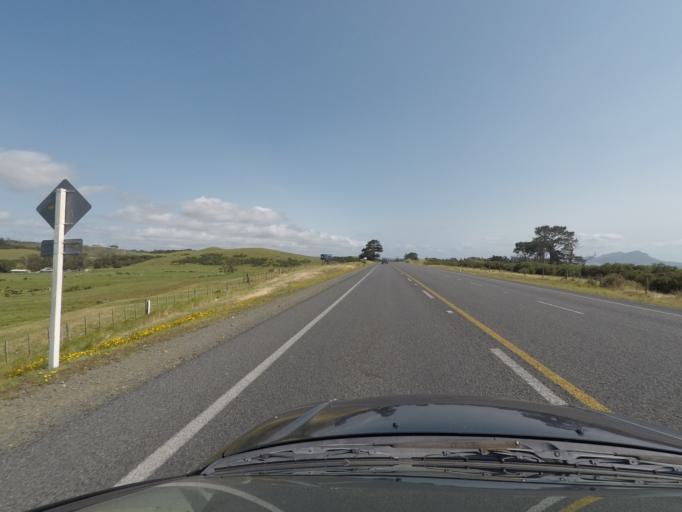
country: NZ
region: Northland
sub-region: Whangarei
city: Ruakaka
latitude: -35.9268
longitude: 174.4541
